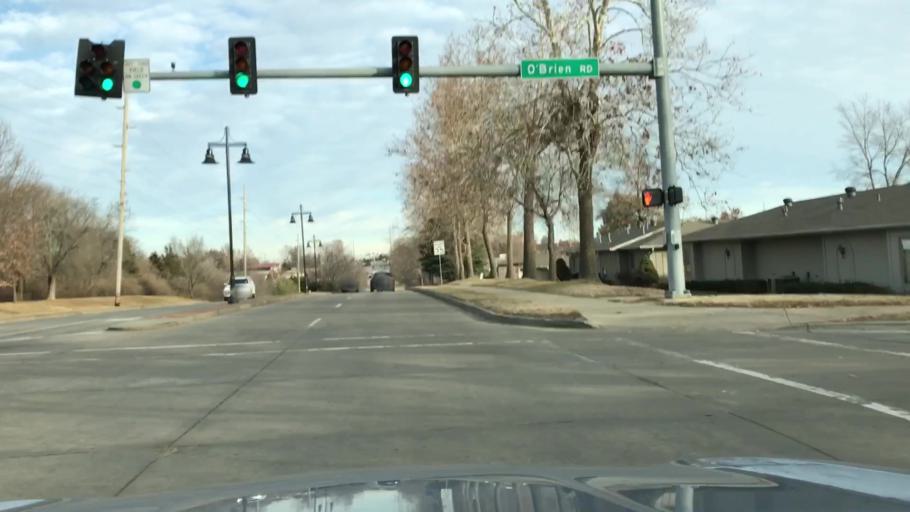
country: US
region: Missouri
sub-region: Jackson County
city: Lees Summit
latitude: 38.9200
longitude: -94.4129
